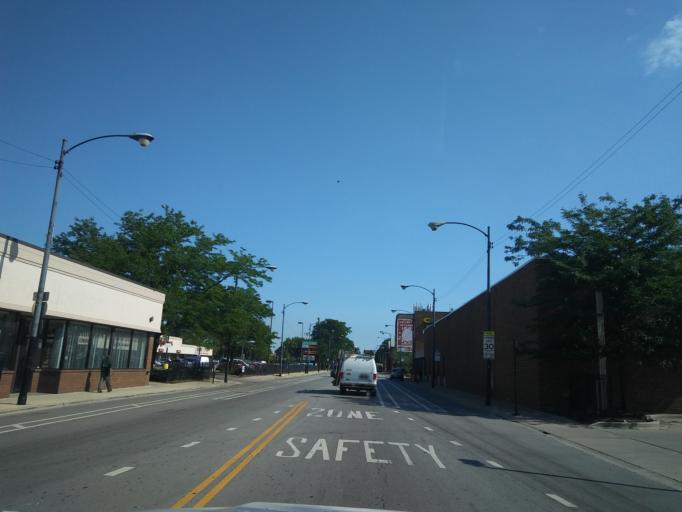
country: US
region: Illinois
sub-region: Cook County
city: Chicago
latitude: 41.8384
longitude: -87.6463
